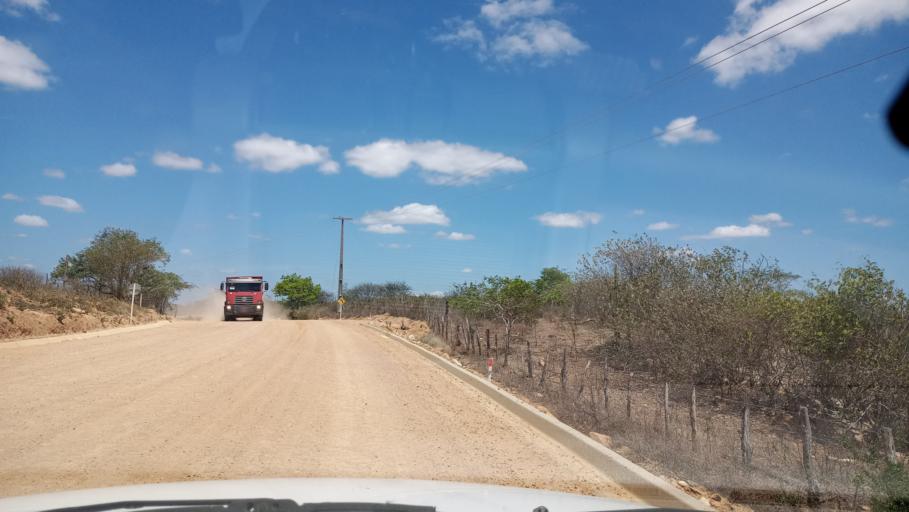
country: BR
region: Rio Grande do Norte
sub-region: Sao Paulo Do Potengi
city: Sao Paulo do Potengi
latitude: -5.7708
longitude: -35.9111
